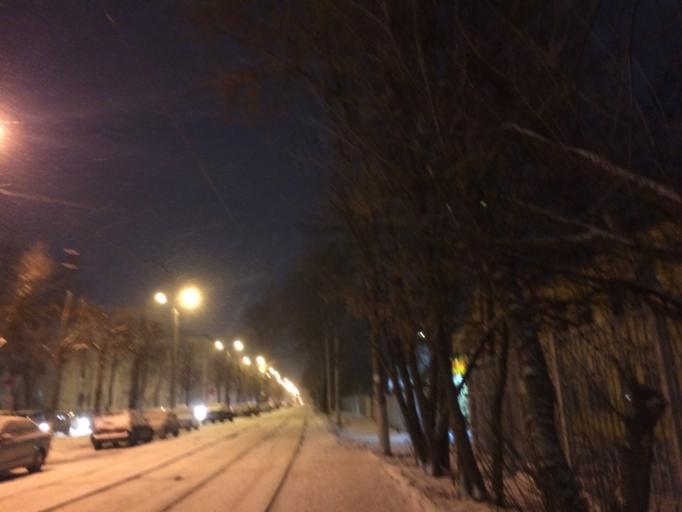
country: RU
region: Tula
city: Tula
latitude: 54.1817
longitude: 37.6008
